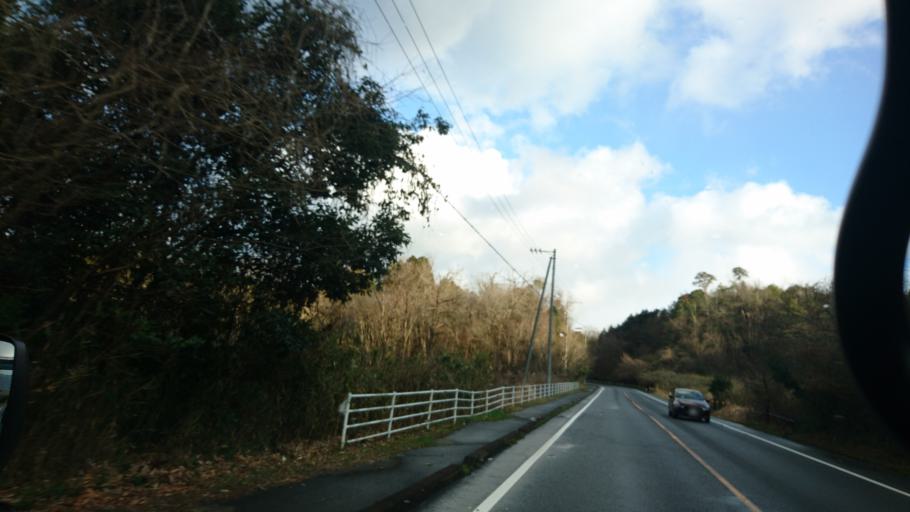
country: JP
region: Mie
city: Ueno-ebisumachi
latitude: 34.7605
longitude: 136.0602
